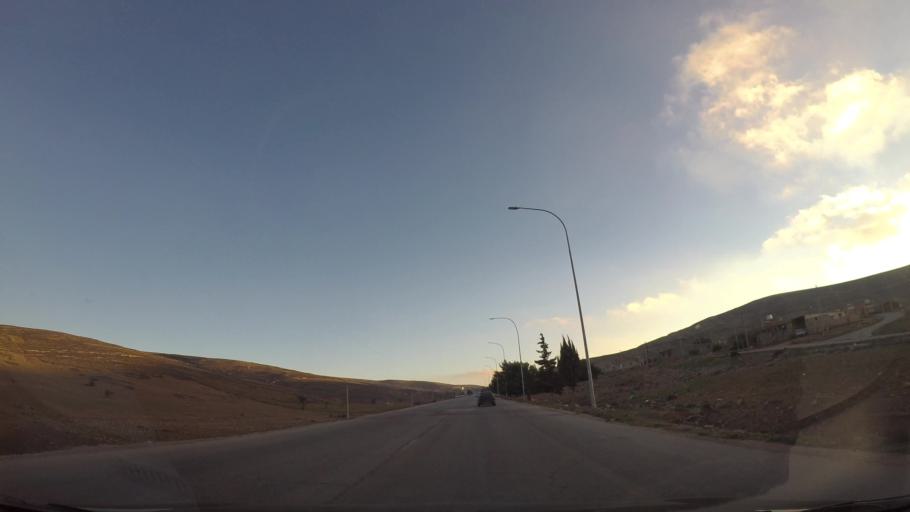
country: JO
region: Ma'an
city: Petra
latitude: 30.4316
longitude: 35.5158
